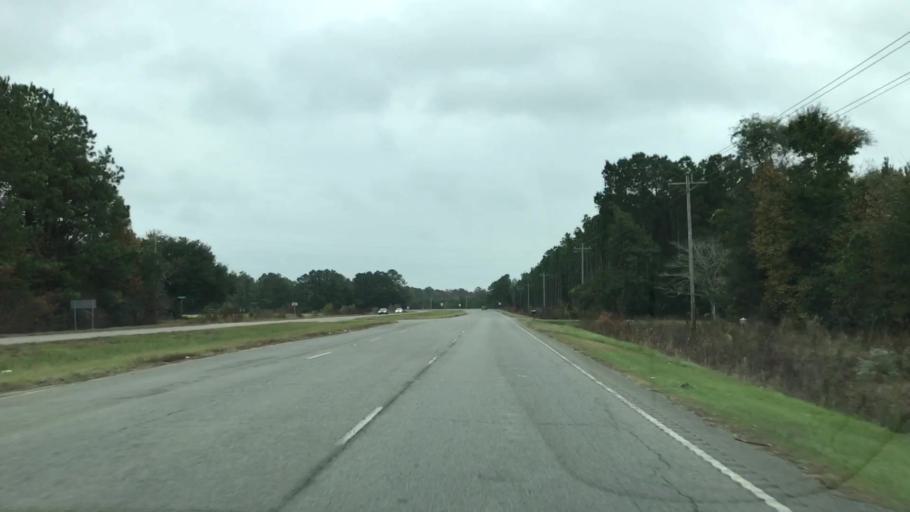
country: US
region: South Carolina
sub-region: Charleston County
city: Awendaw
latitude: 33.0386
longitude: -79.6002
